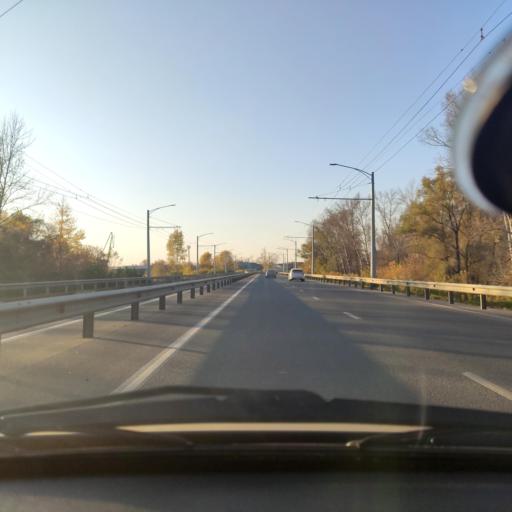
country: RU
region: Bashkortostan
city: Mikhaylovka
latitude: 54.7743
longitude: 55.8968
